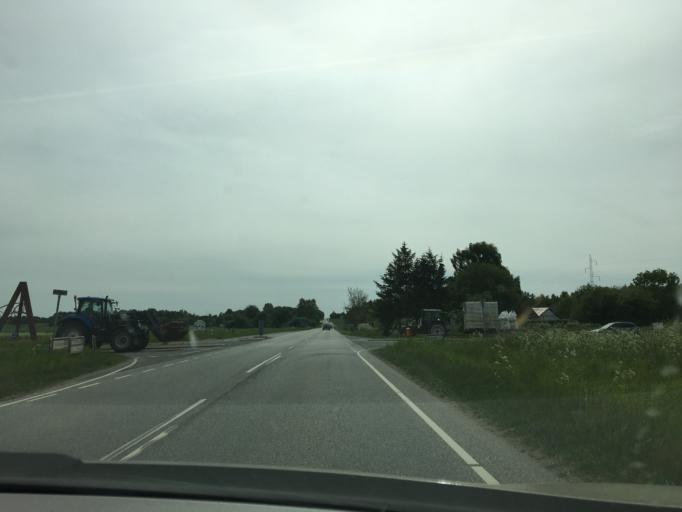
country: DK
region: Central Jutland
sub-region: Norddjurs Kommune
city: Allingabro
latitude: 56.4652
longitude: 10.3056
